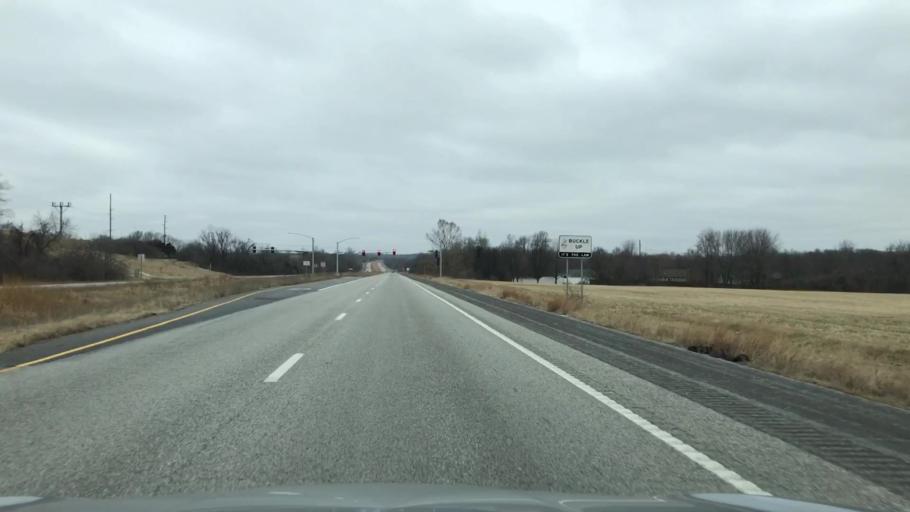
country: US
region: Missouri
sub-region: Clay County
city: Liberty
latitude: 39.2046
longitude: -94.4039
